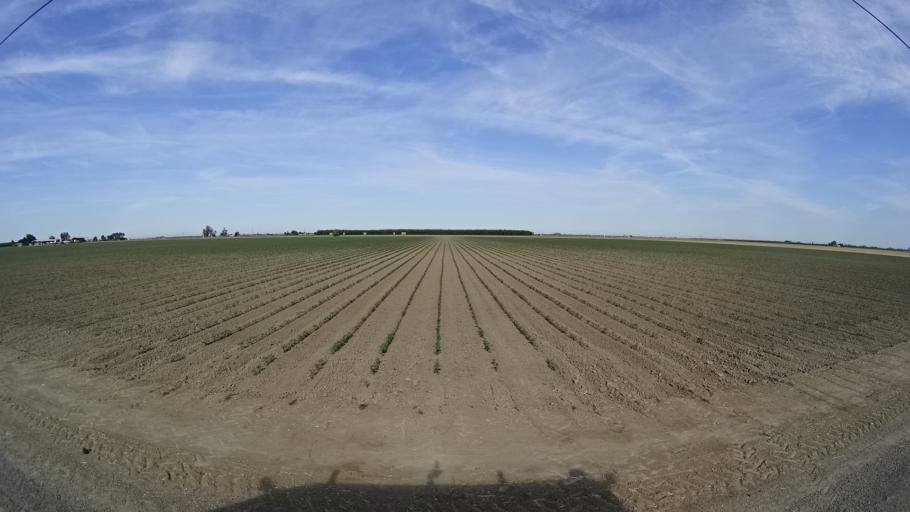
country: US
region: California
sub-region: Kings County
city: Hanford
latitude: 36.3779
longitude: -119.5469
